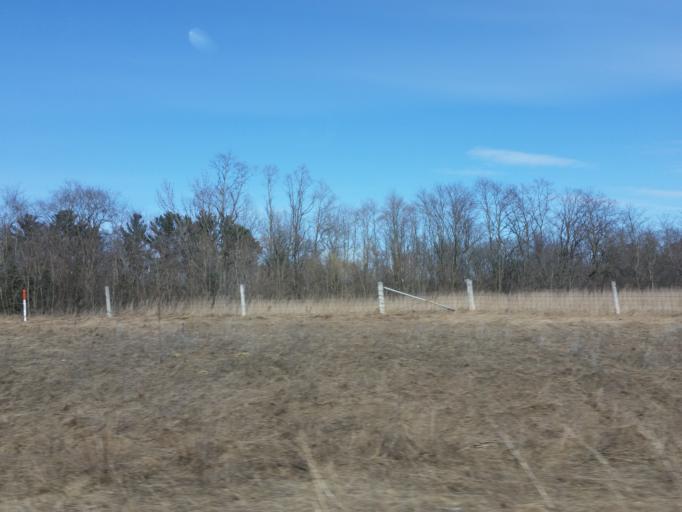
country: US
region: Wisconsin
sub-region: Eau Claire County
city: Altoona
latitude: 44.7544
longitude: -91.3915
